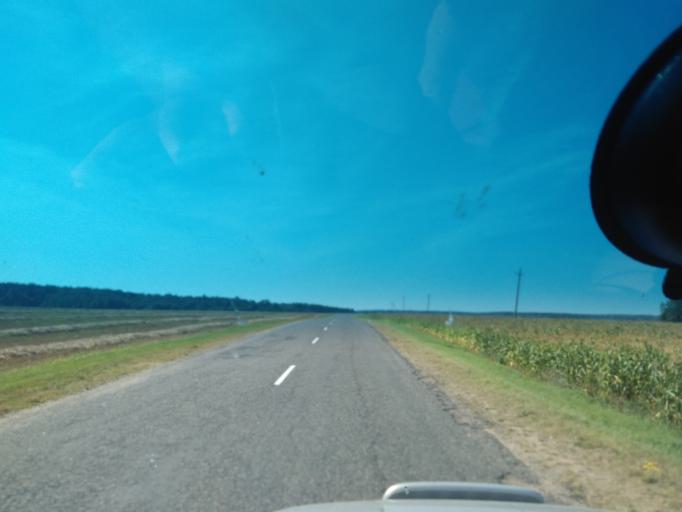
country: BY
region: Minsk
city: Kapyl'
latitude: 53.2198
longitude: 27.1505
